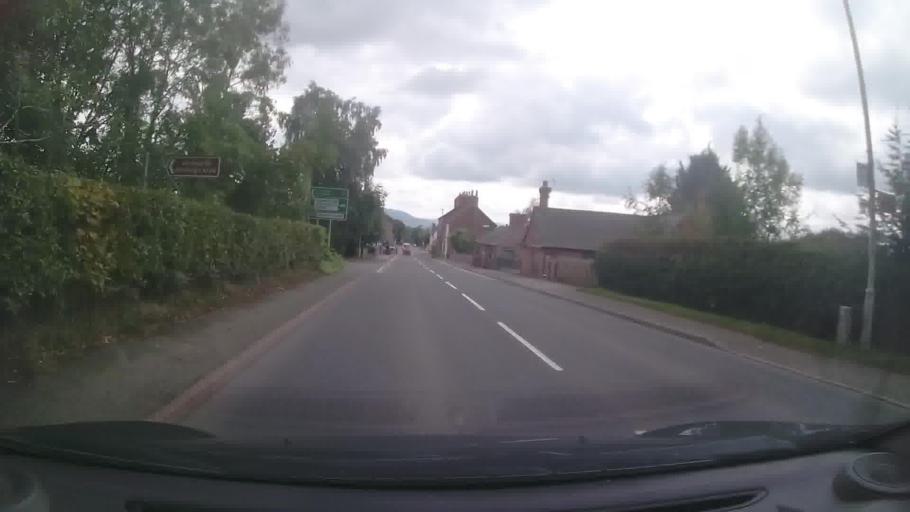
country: GB
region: England
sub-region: Shropshire
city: Pant
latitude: 52.7825
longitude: -3.0893
